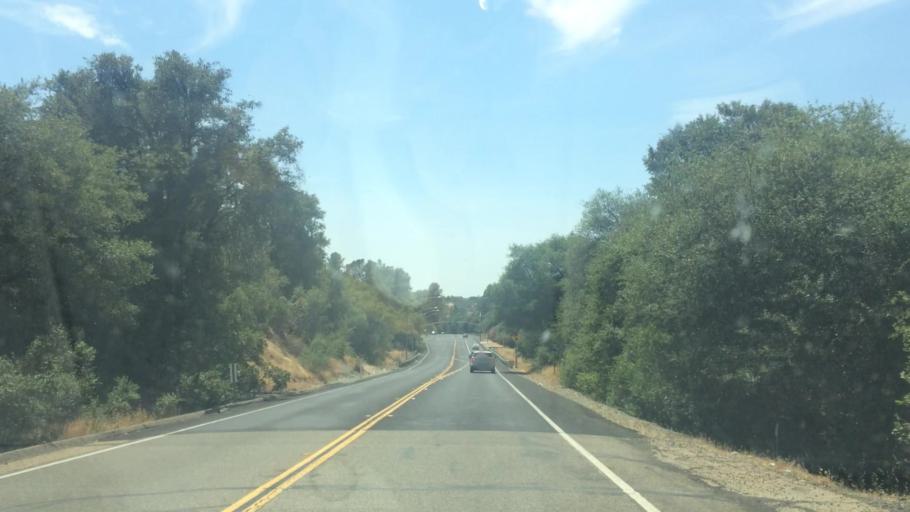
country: US
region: California
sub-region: Amador County
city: Jackson
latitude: 38.4016
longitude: -120.7288
